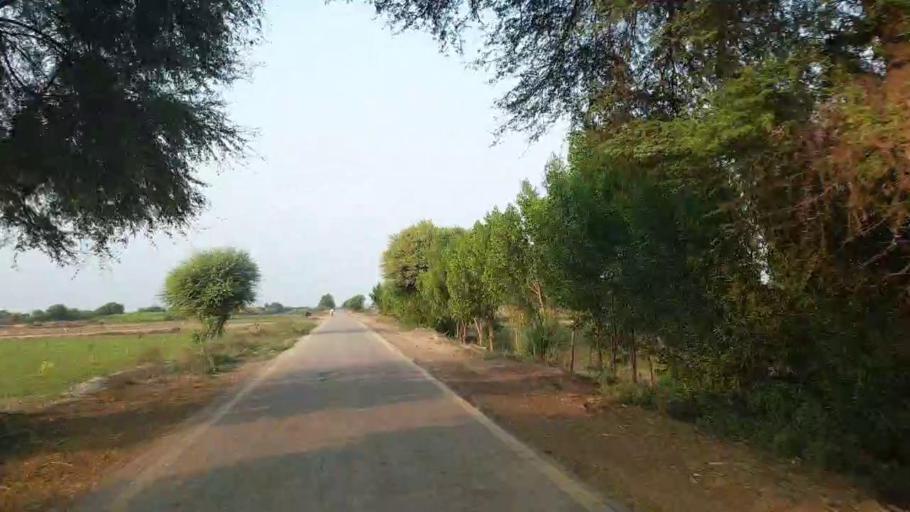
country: PK
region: Sindh
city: Tando Ghulam Ali
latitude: 25.0833
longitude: 68.9585
